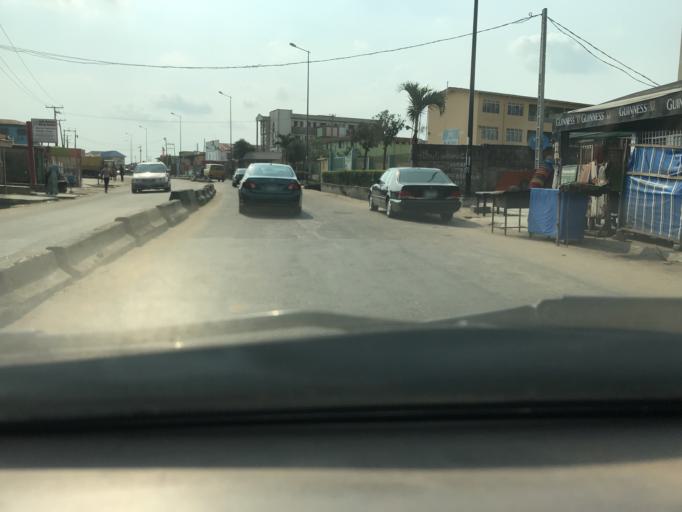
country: NG
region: Lagos
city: Agege
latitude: 6.6004
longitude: 3.2965
